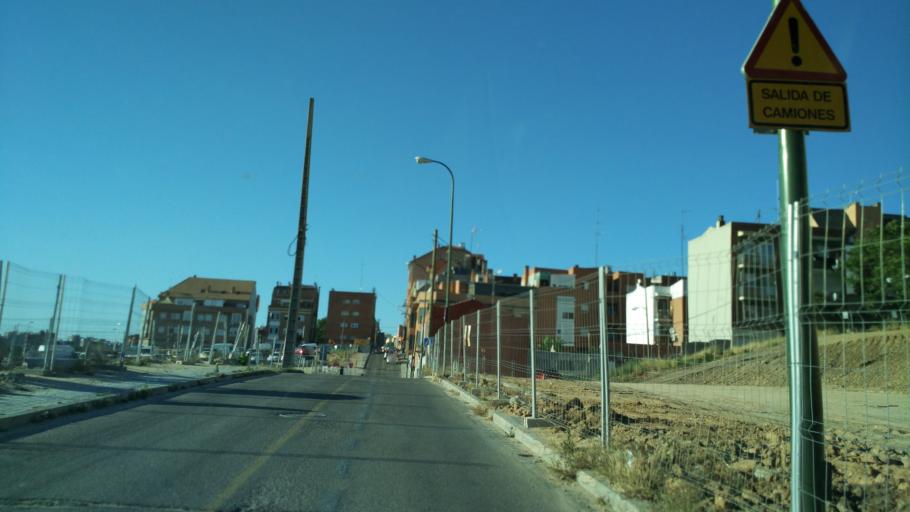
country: ES
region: Madrid
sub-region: Provincia de Madrid
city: Tetuan de las Victorias
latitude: 40.4664
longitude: -3.7078
